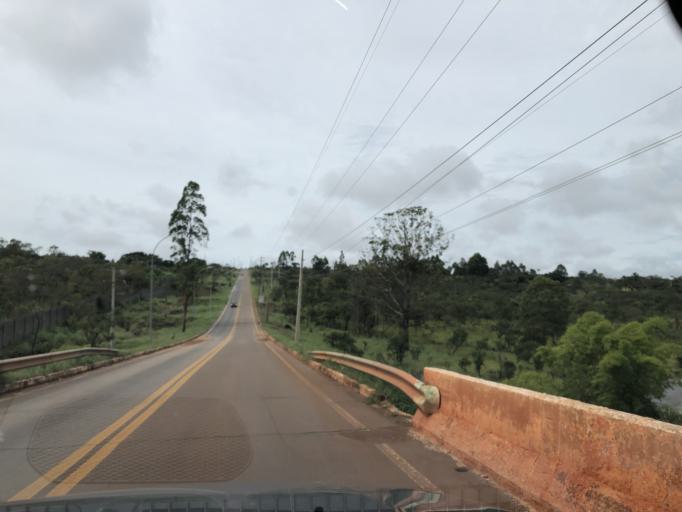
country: BR
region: Federal District
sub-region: Brasilia
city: Brasilia
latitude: -15.7696
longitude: -48.1286
